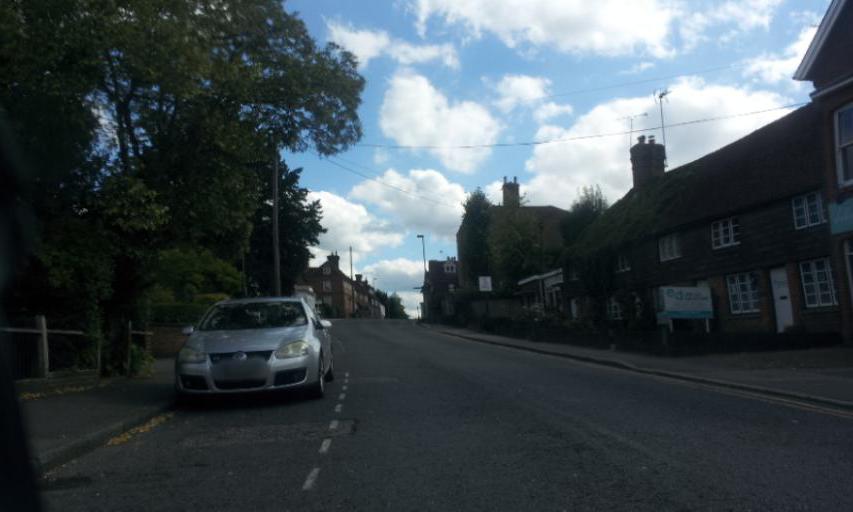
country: GB
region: England
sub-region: Kent
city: Staplehurst
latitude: 51.1597
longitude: 0.5524
